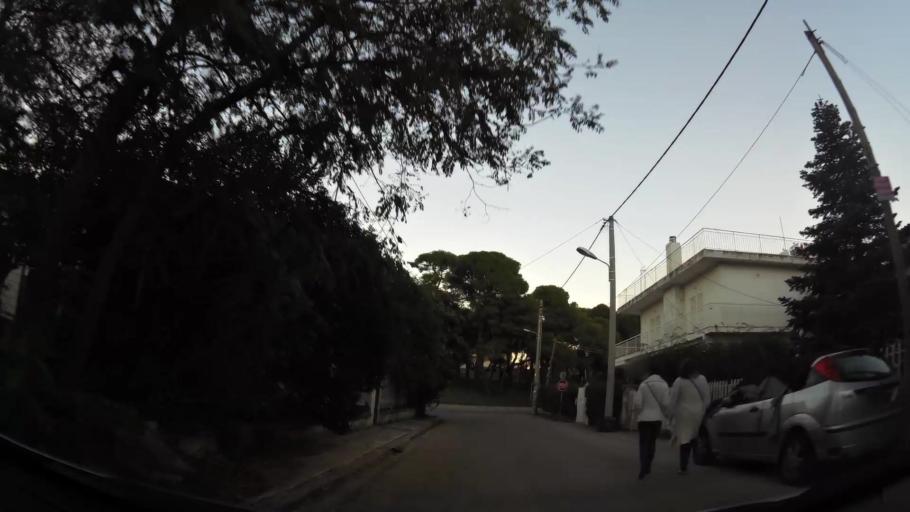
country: GR
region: Attica
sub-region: Nomarchia Athinas
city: Lykovrysi
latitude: 38.0670
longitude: 23.7889
